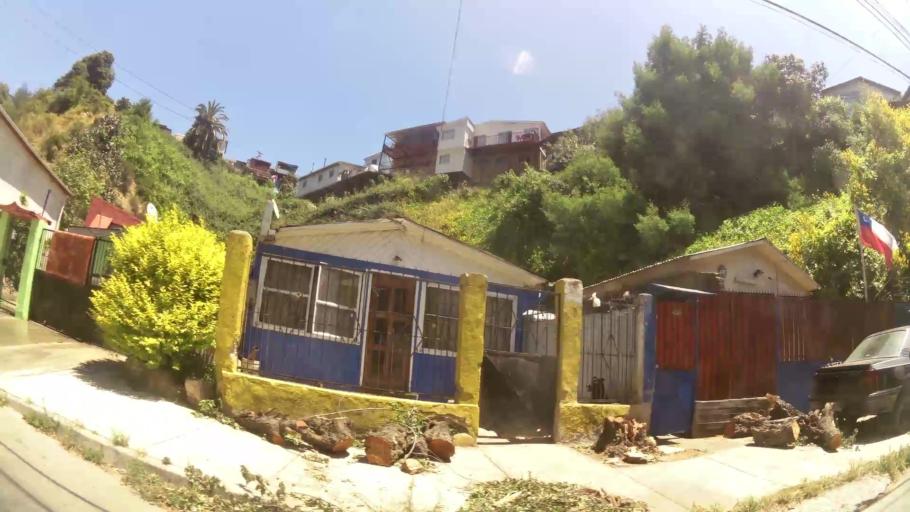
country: CL
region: Valparaiso
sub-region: Provincia de Valparaiso
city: Valparaiso
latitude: -33.0379
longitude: -71.6381
